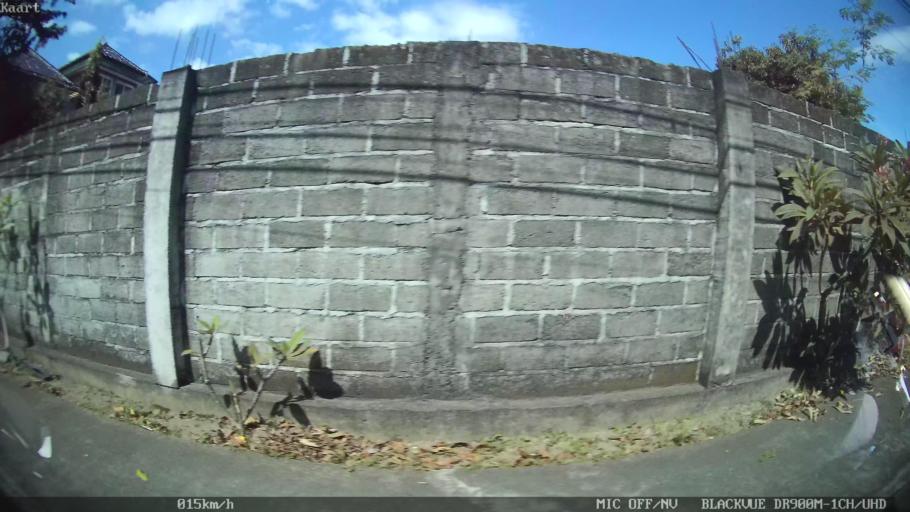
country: ID
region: Bali
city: Banjar Kertasari
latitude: -8.6424
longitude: 115.1794
